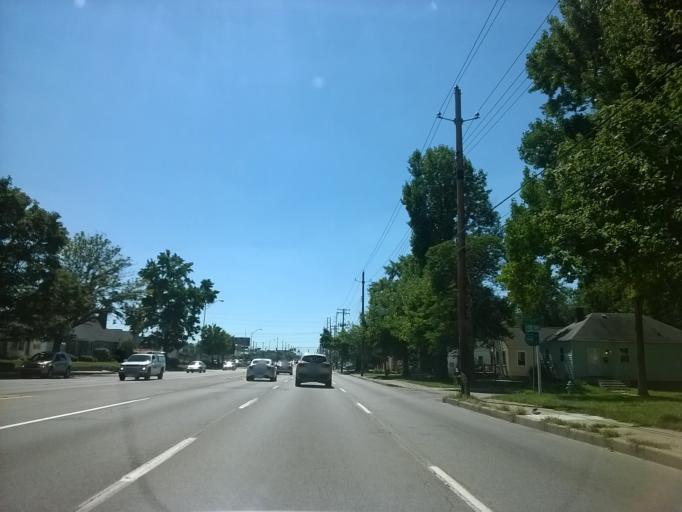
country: US
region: Indiana
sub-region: Marion County
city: Broad Ripple
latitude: 39.8569
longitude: -86.1223
